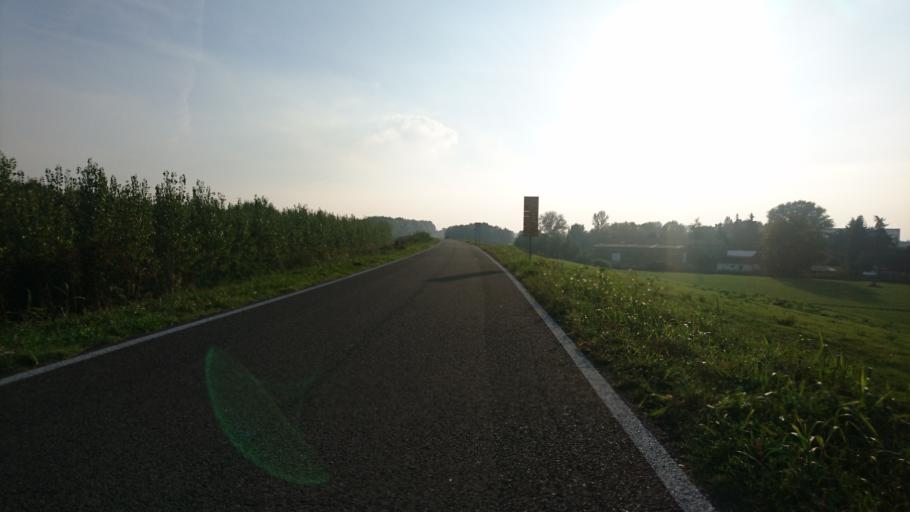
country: IT
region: Emilia-Romagna
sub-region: Provincia di Ferrara
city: Francolino
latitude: 44.9080
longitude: 11.6521
